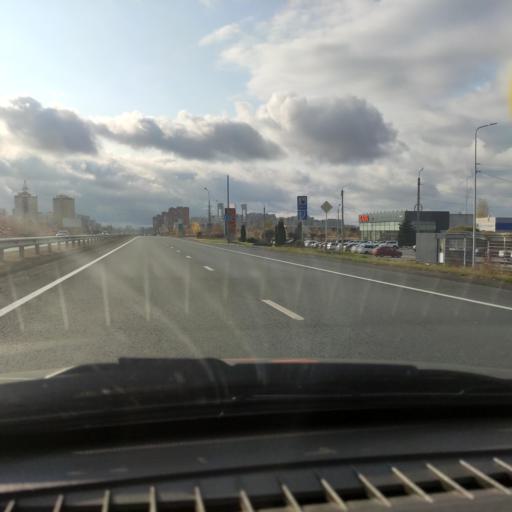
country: RU
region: Samara
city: Tol'yatti
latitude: 53.5522
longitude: 49.3382
